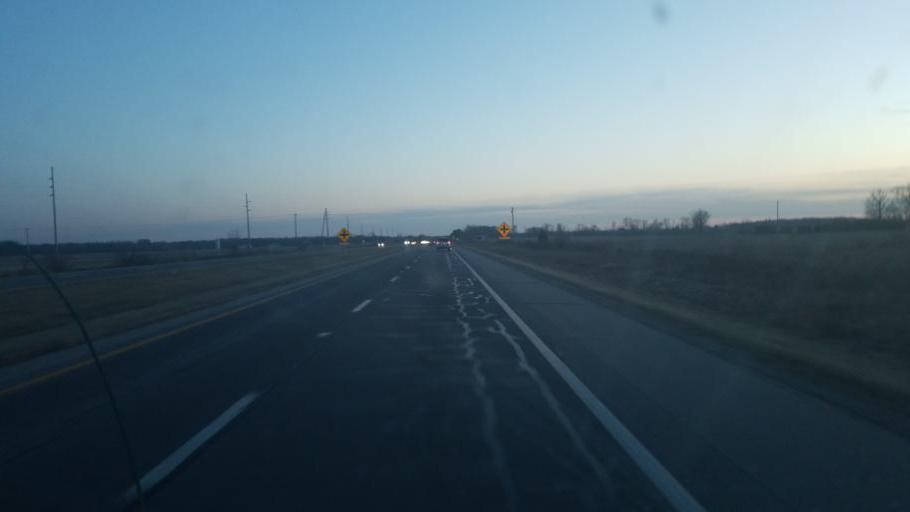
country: US
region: Ohio
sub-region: Marion County
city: Marion
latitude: 40.4863
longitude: -83.0748
